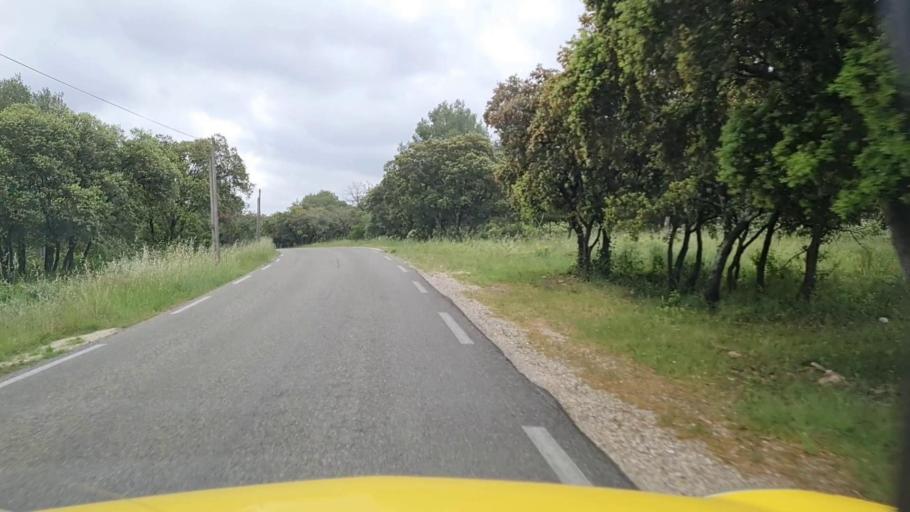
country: FR
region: Languedoc-Roussillon
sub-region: Departement du Gard
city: Langlade
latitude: 43.7913
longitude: 4.2605
